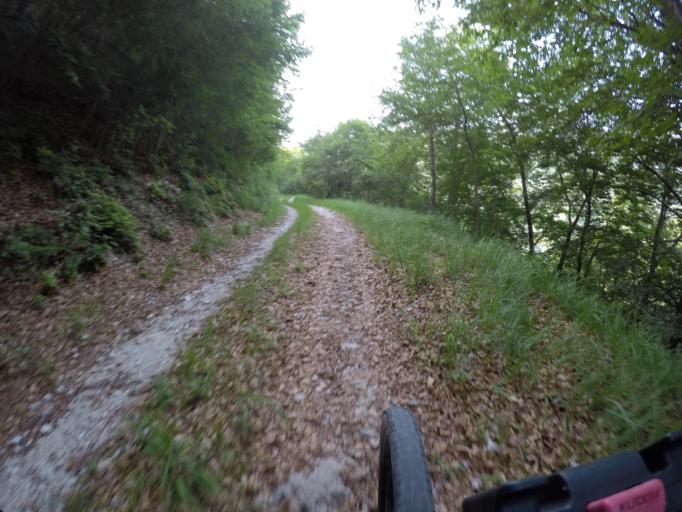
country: IT
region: Friuli Venezia Giulia
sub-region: Provincia di Udine
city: Resiutta
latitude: 46.3274
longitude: 13.2244
